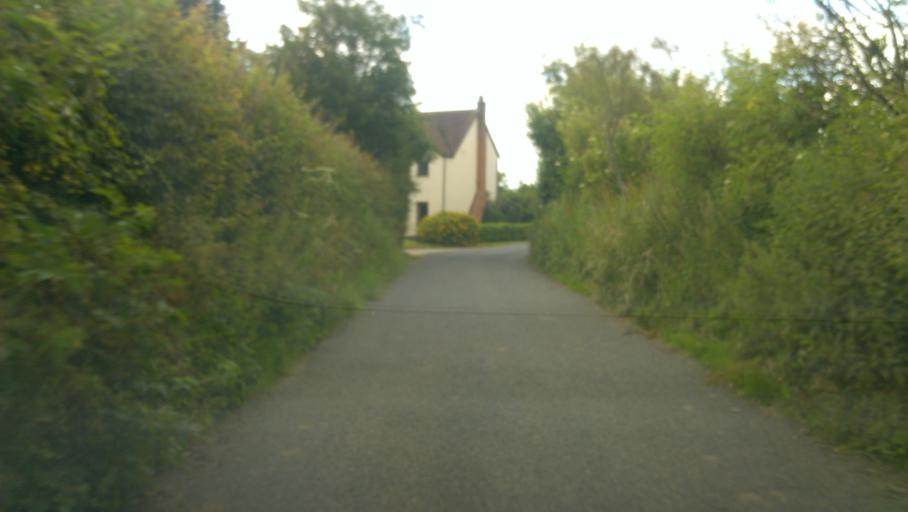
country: GB
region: England
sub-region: Essex
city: Coggeshall
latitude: 51.8627
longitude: 0.6350
